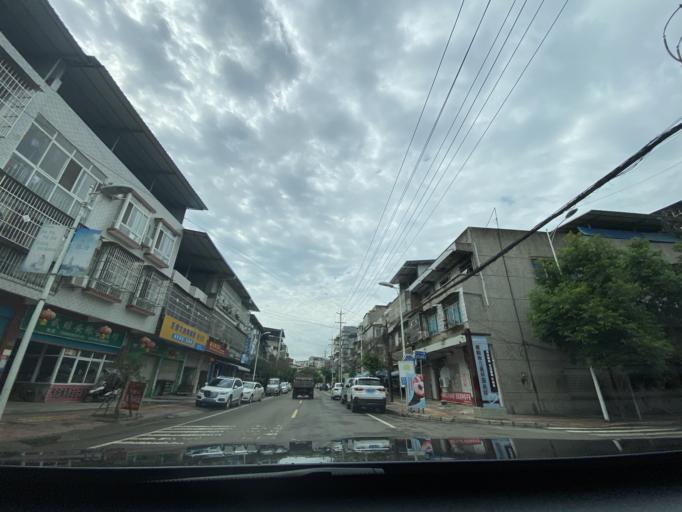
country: CN
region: Sichuan
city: Jiancheng
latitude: 30.4306
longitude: 104.6384
